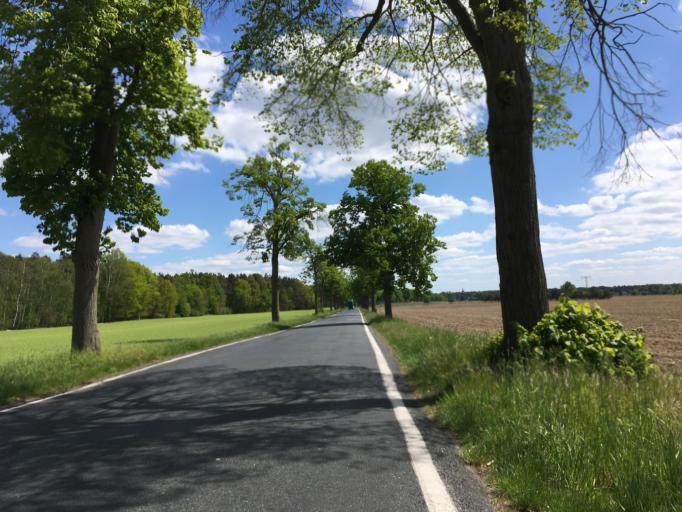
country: DE
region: Brandenburg
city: Wandlitz
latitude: 52.7839
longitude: 13.4212
